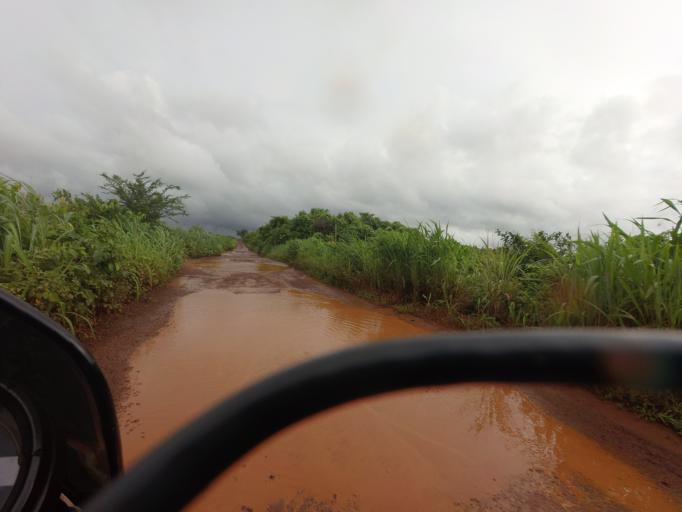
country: SL
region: Northern Province
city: Kukuna
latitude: 9.3381
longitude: -12.6667
